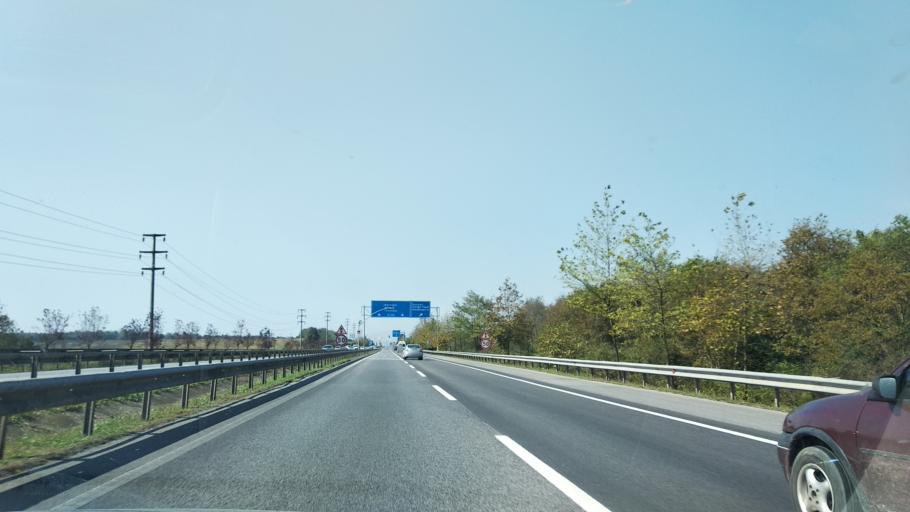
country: TR
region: Kocaeli
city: Derbent
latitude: 40.7425
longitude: 30.0852
